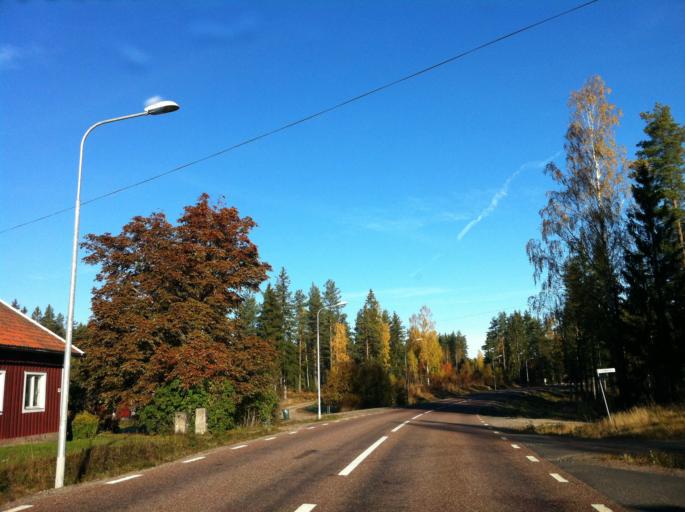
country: SE
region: Gaevleborg
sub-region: Gavle Kommun
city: Gavle
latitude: 60.5564
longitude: 17.1227
